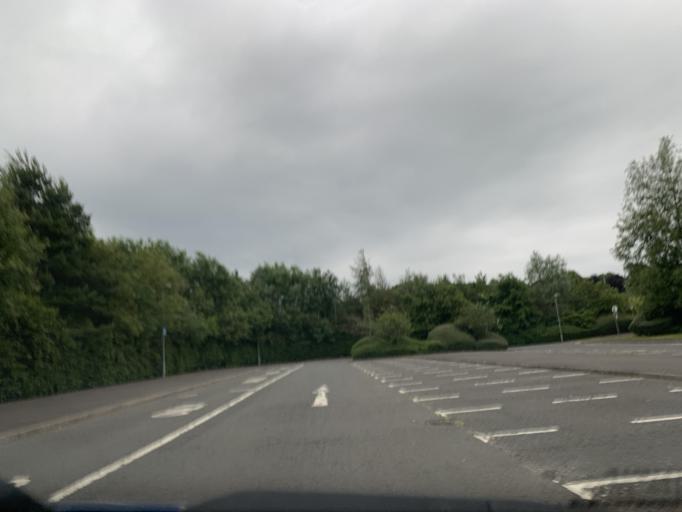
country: GB
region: Scotland
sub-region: East Renfrewshire
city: Newton Mearns
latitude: 55.7684
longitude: -4.3453
